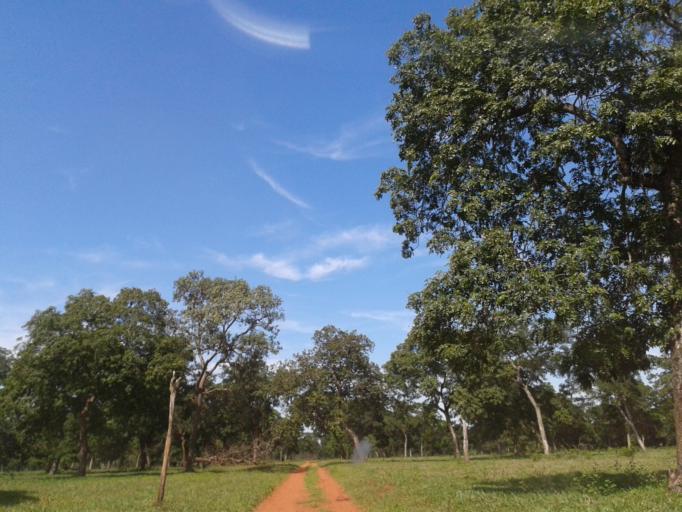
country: BR
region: Minas Gerais
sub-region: Santa Vitoria
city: Santa Vitoria
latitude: -19.1624
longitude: -50.5087
